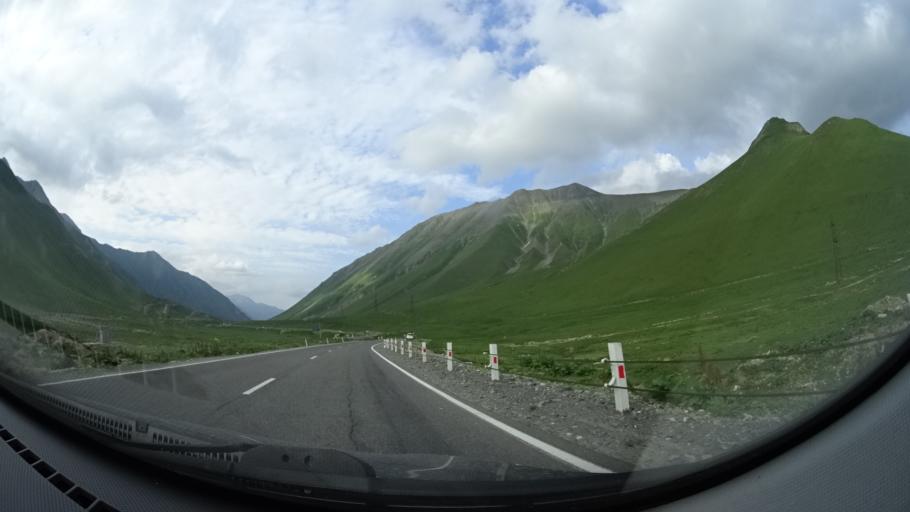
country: GE
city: Gudauri
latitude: 42.5071
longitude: 44.4578
